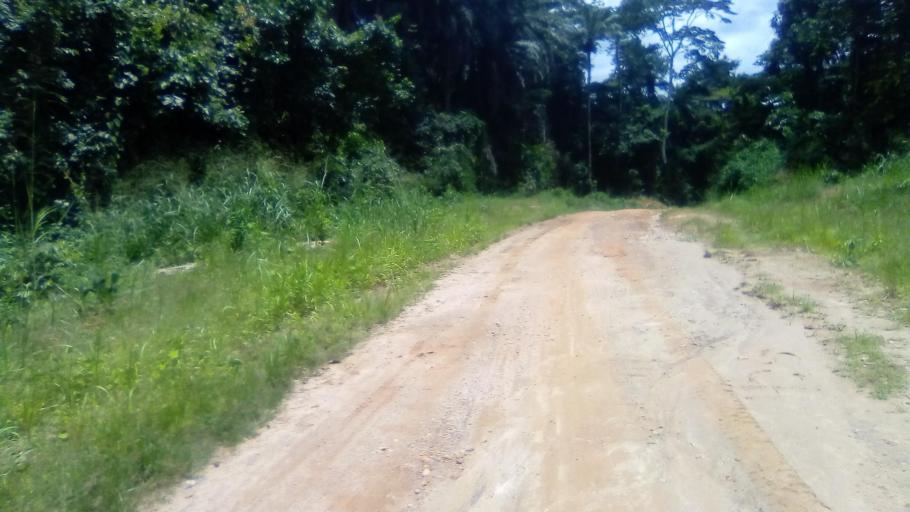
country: SL
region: Eastern Province
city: Simbakoro
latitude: 8.5293
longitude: -10.9105
